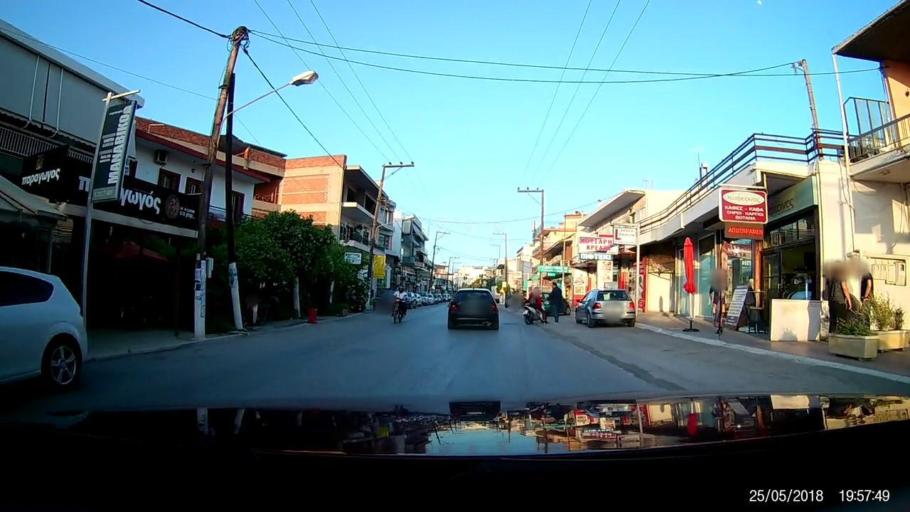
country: GR
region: Central Greece
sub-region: Nomos Evvoias
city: Vasilikon
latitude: 38.4260
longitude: 23.6693
